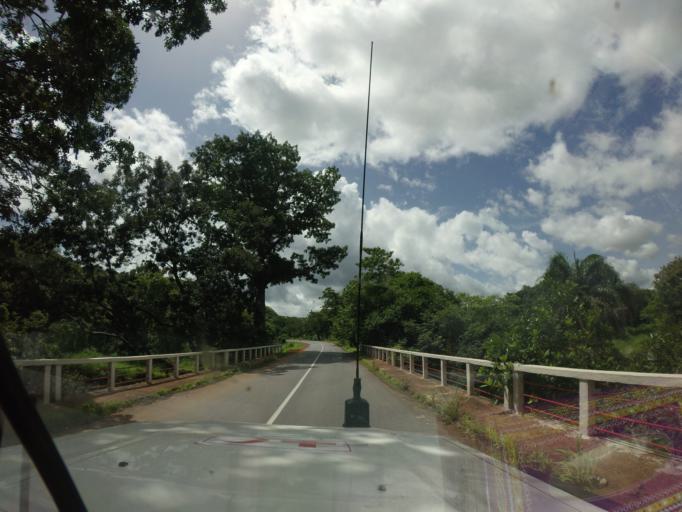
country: SL
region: Northern Province
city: Bindi
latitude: 10.1556
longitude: -11.6748
